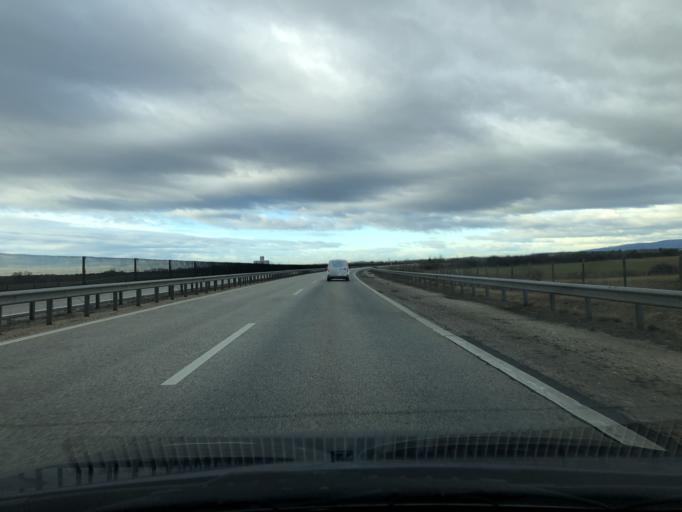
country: HU
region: Vas
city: Vep
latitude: 47.2735
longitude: 16.7925
